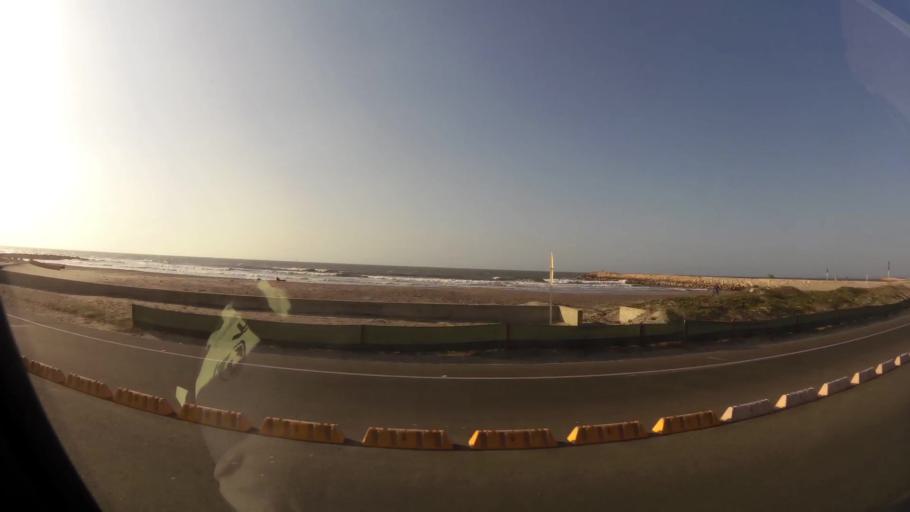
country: CO
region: Bolivar
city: Cartagena
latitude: 10.4399
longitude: -75.5298
